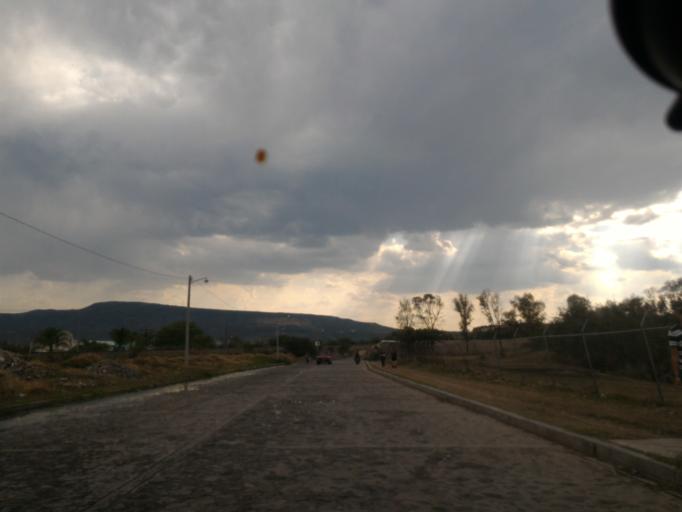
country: MX
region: Guanajuato
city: San Francisco del Rincon
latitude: 21.0387
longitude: -101.8572
